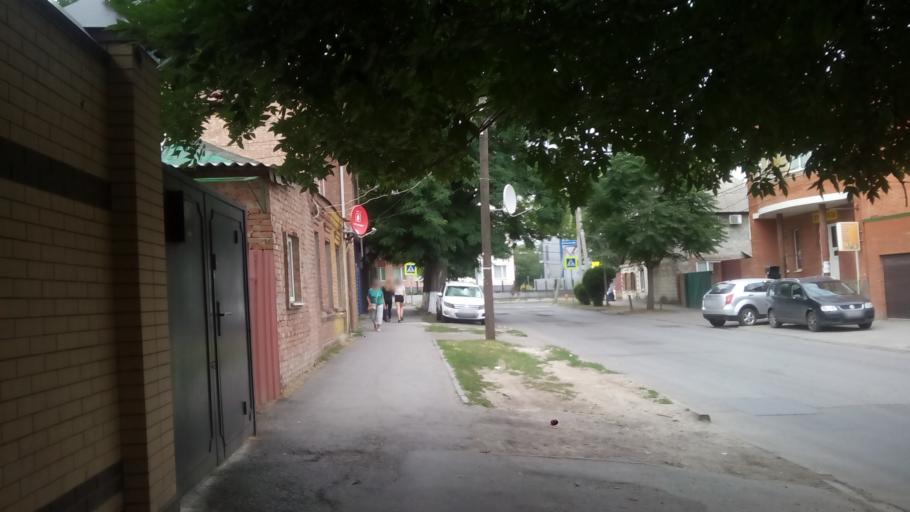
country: RU
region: Rostov
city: Rostov-na-Donu
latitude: 47.2131
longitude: 39.6742
